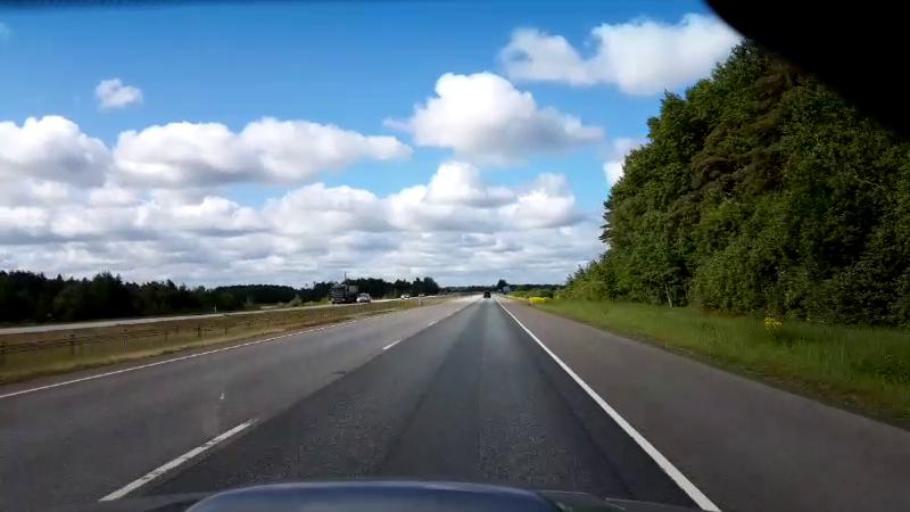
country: EE
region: Harju
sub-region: Saue linn
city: Saue
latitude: 59.2785
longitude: 24.5261
